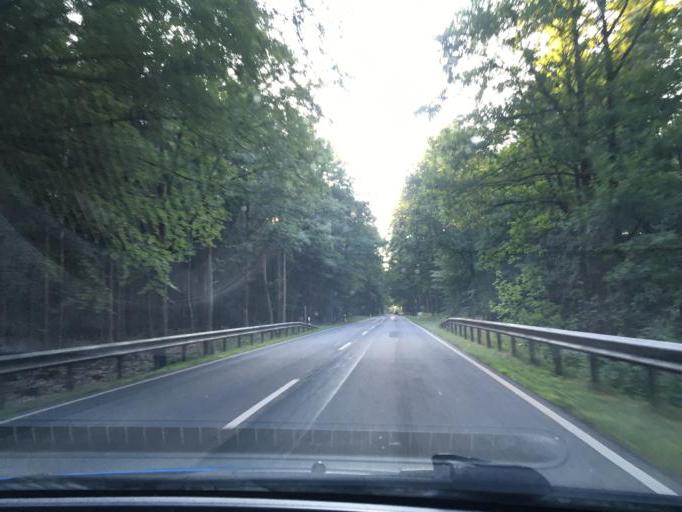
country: DE
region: Lower Saxony
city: Unterluss
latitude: 52.8102
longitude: 10.3574
